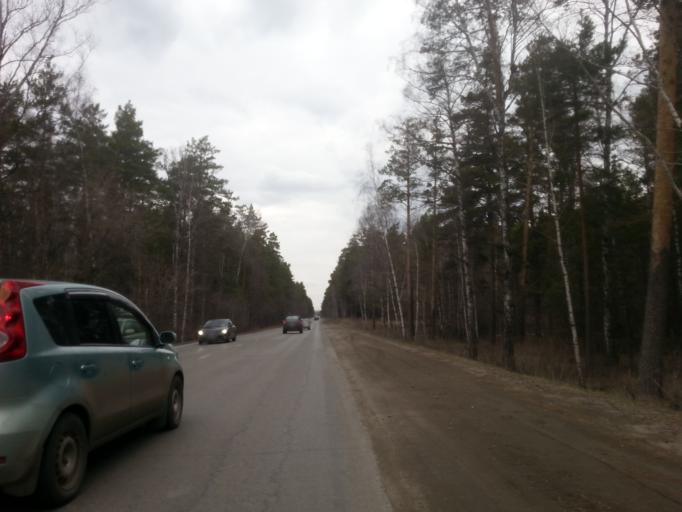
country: RU
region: Altai Krai
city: Yuzhnyy
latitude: 53.2764
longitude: 83.7201
